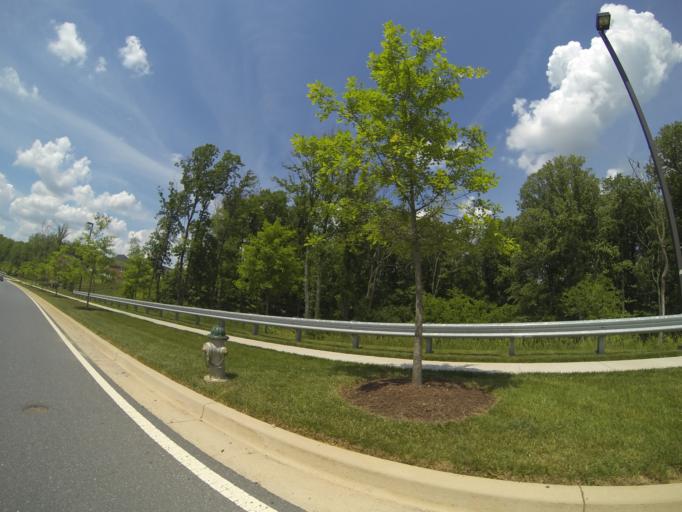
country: US
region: Maryland
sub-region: Montgomery County
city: Clarksburg
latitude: 39.2303
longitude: -77.2533
